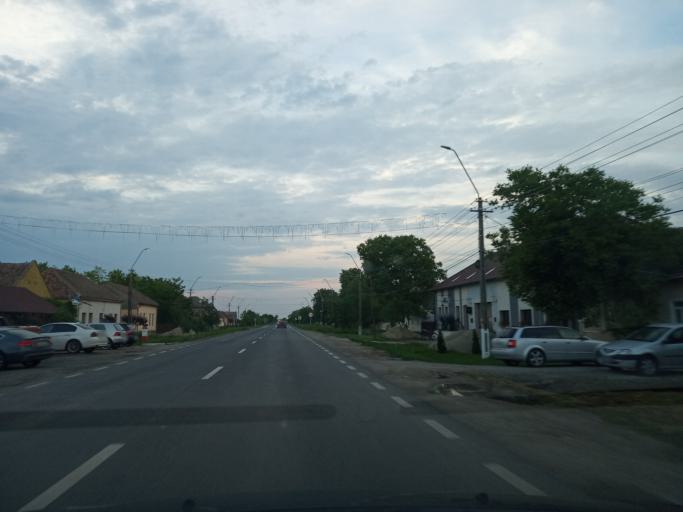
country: RO
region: Timis
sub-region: Comuna Voiteg
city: Voiteg
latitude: 45.4715
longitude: 21.2345
